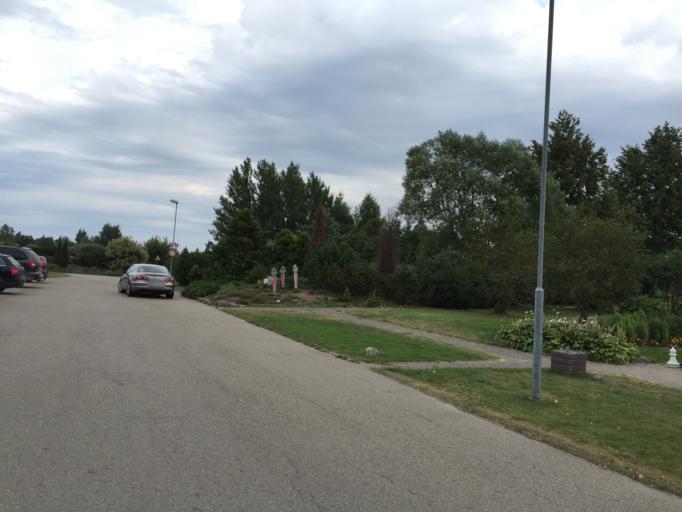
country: LV
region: Jurmala
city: Jurmala
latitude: 56.8967
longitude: 23.7167
